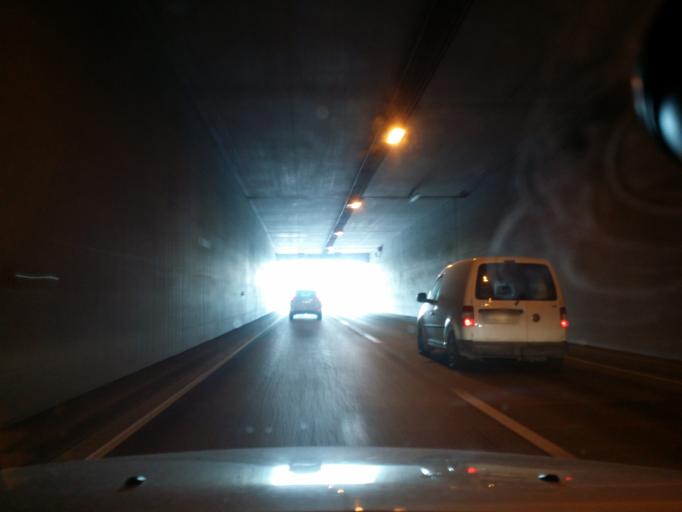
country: SE
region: Stockholm
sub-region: Stockholms Kommun
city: Kista
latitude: 59.3992
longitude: 17.8995
